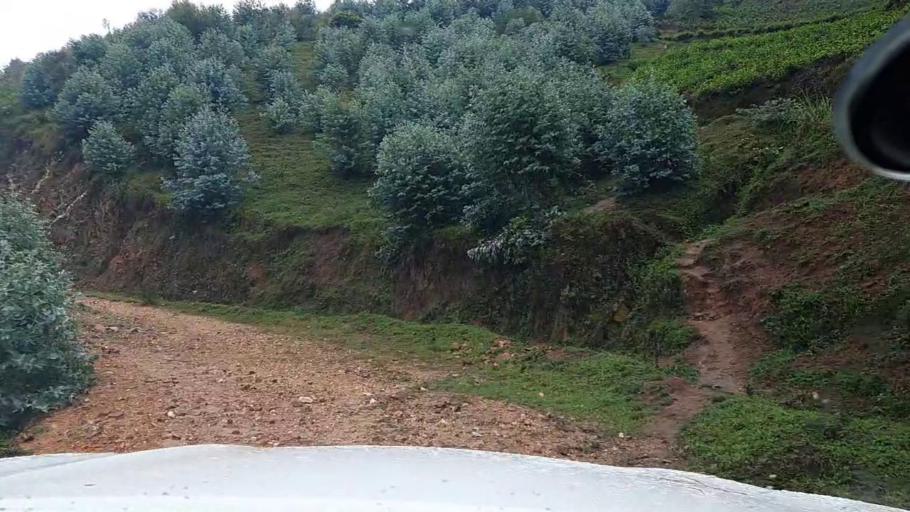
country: RW
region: Western Province
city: Kibuye
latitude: -2.1394
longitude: 29.4580
